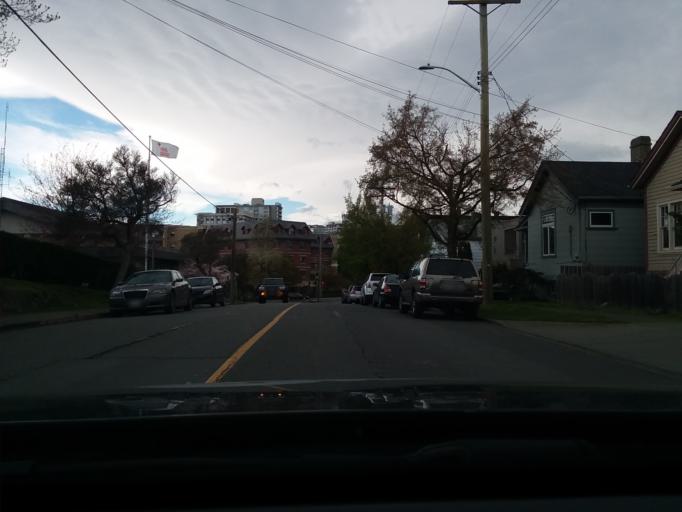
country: CA
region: British Columbia
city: Victoria
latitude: 48.4191
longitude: -123.3595
